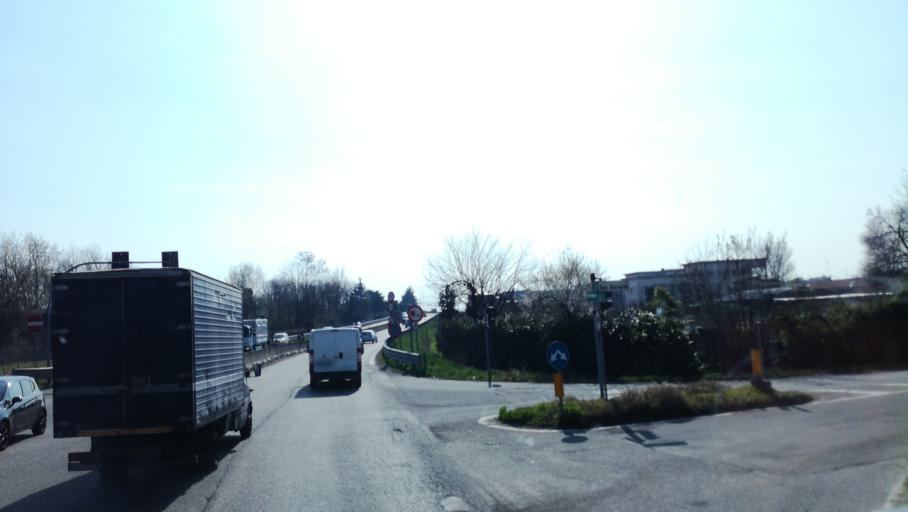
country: IT
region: Lombardy
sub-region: Citta metropolitana di Milano
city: Passirana
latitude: 45.5380
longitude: 9.0463
